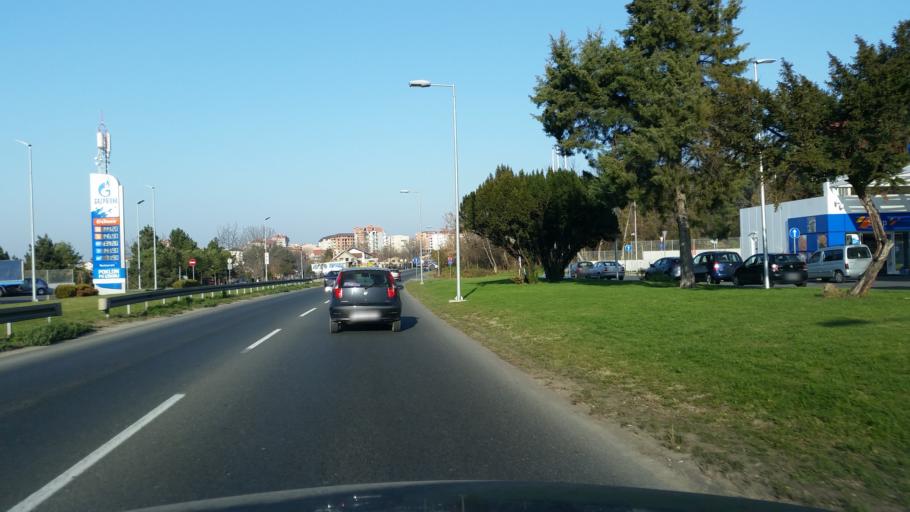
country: RS
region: Central Serbia
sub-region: Belgrade
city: Rakovica
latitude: 44.7513
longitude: 20.4125
